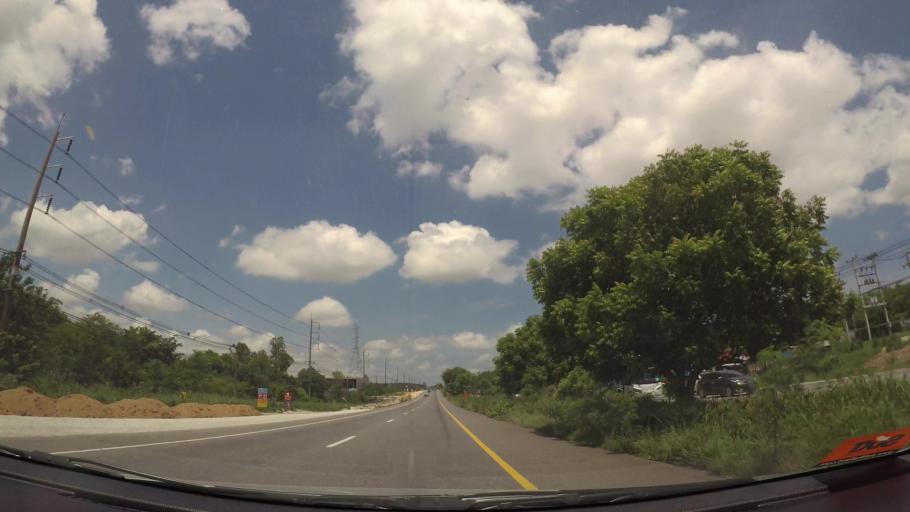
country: TH
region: Rayong
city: Nikhom Phattana
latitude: 12.7639
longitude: 101.1812
